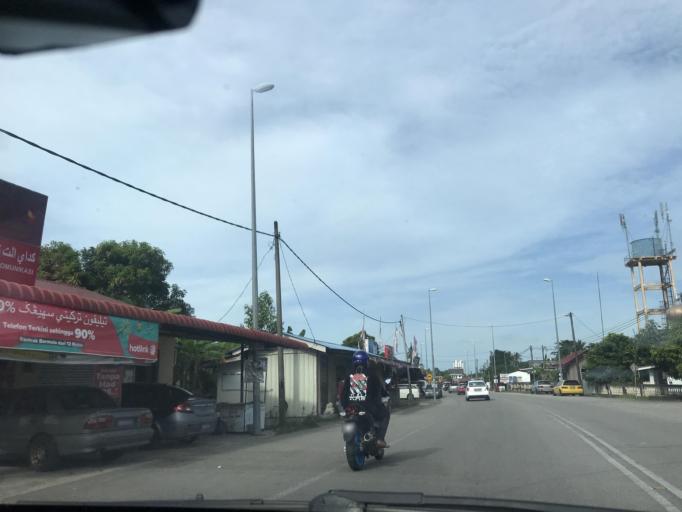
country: MY
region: Kelantan
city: Kota Bharu
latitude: 6.1378
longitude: 102.2146
